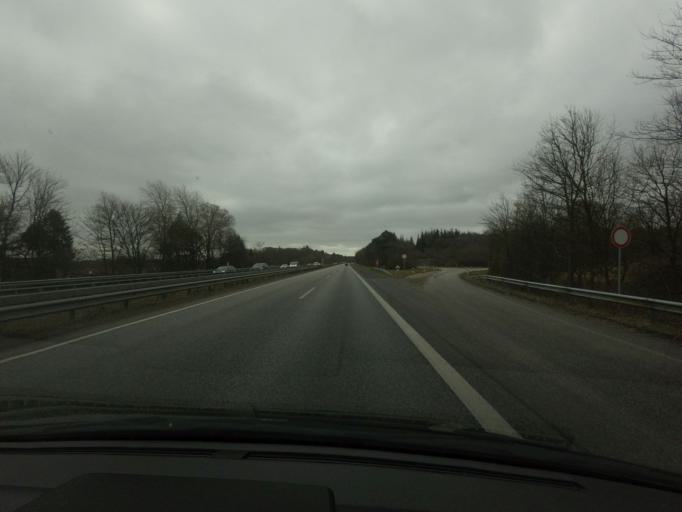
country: DE
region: Schleswig-Holstein
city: Handewitt
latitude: 54.7609
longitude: 9.3606
